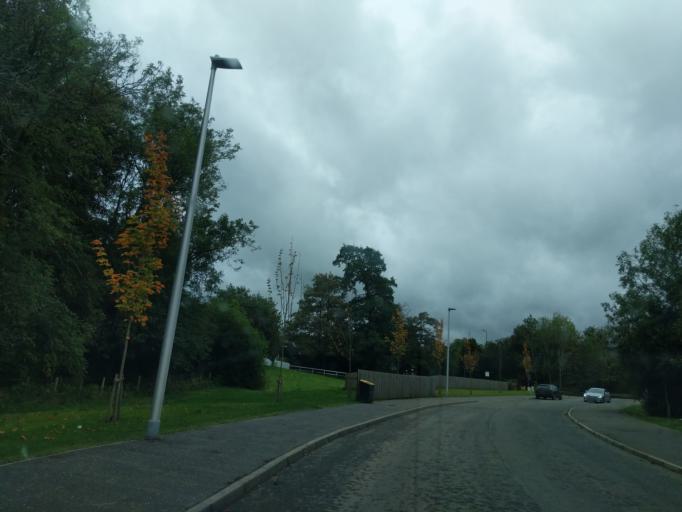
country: GB
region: Scotland
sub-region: Edinburgh
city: Balerno
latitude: 55.8898
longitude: -3.3351
